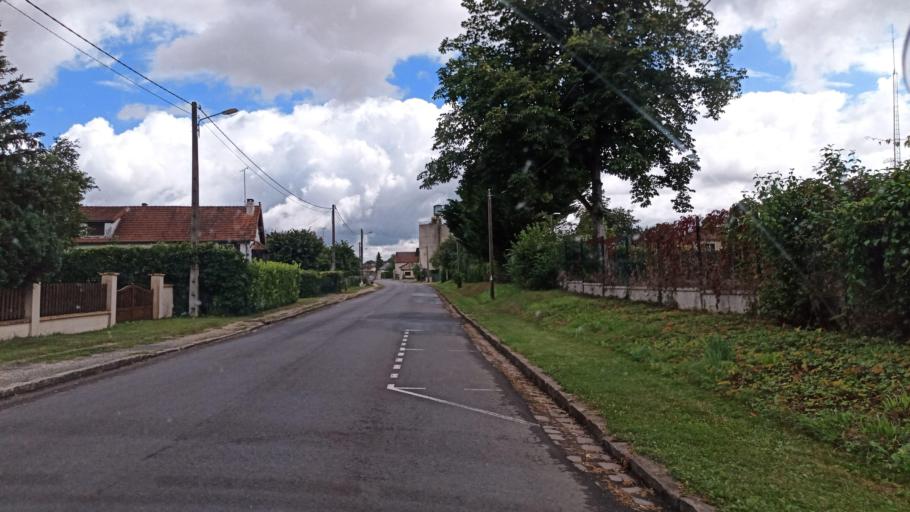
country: FR
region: Ile-de-France
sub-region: Departement de Seine-et-Marne
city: Voulx
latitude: 48.2818
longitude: 2.9615
